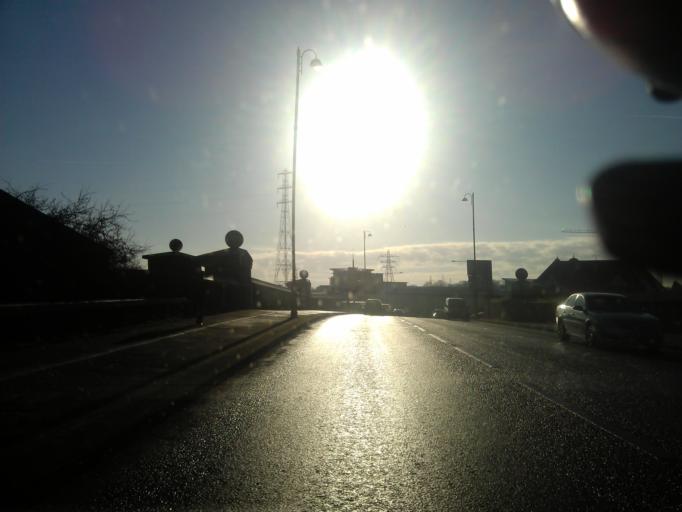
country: GB
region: England
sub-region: Essex
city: Rowhedge
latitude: 51.8827
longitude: 0.9325
